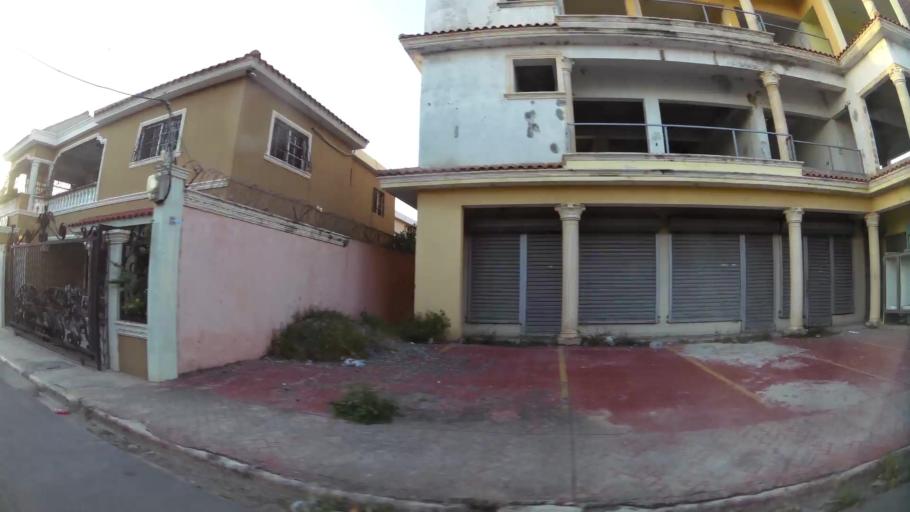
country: DO
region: Santo Domingo
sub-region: Santo Domingo
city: Santo Domingo Este
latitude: 18.4857
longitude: -69.8212
